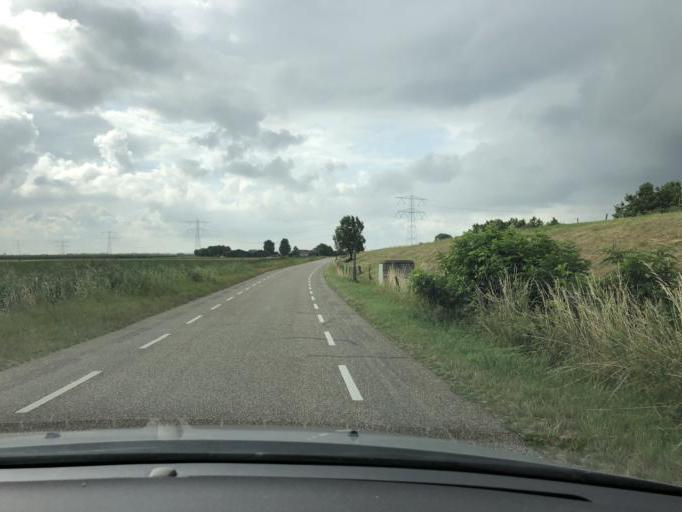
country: NL
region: Zeeland
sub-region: Gemeente Reimerswaal
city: Yerseke
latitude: 51.4551
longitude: 4.0755
